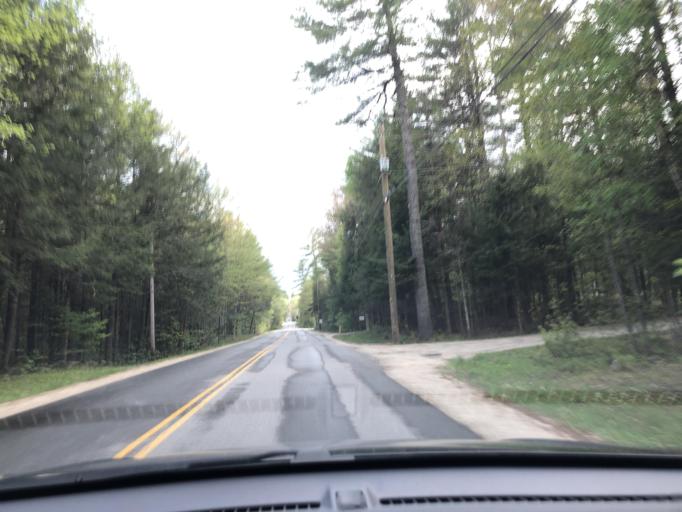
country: US
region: New Hampshire
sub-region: Merrimack County
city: New London
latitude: 43.4078
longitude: -72.0125
